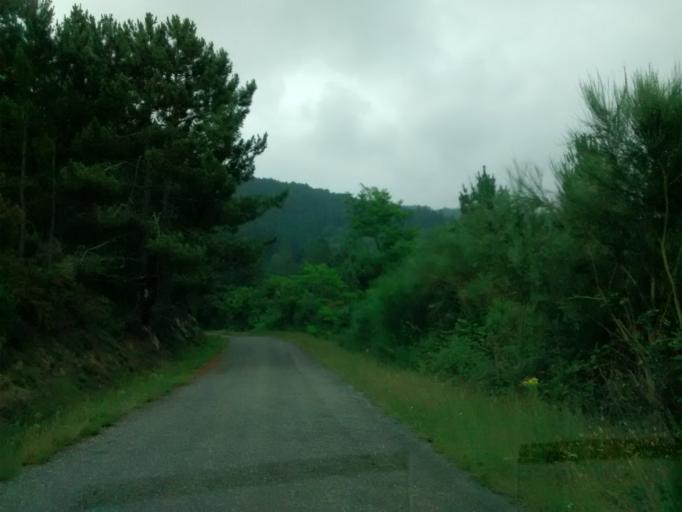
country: ES
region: Galicia
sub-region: Provincia de Ourense
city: Castro Caldelas
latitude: 42.4138
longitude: -7.3906
